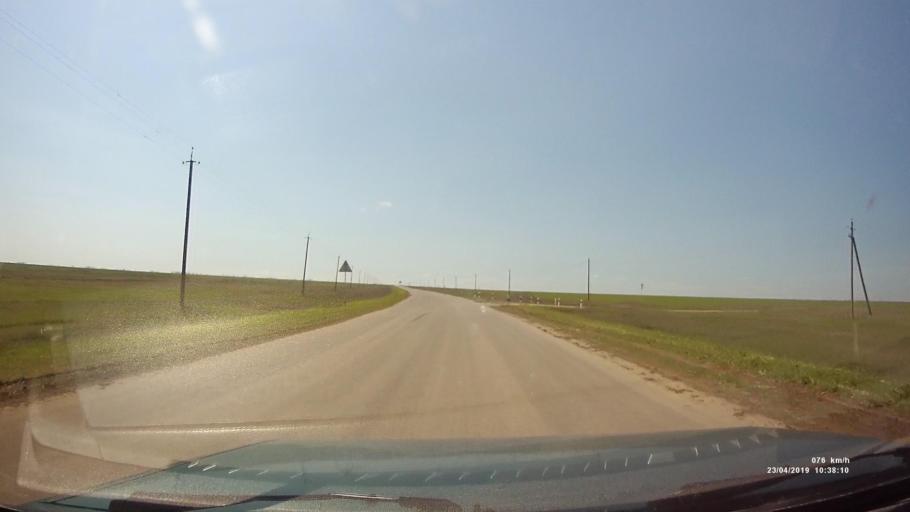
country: RU
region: Kalmykiya
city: Yashalta
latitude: 46.5355
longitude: 42.6389
